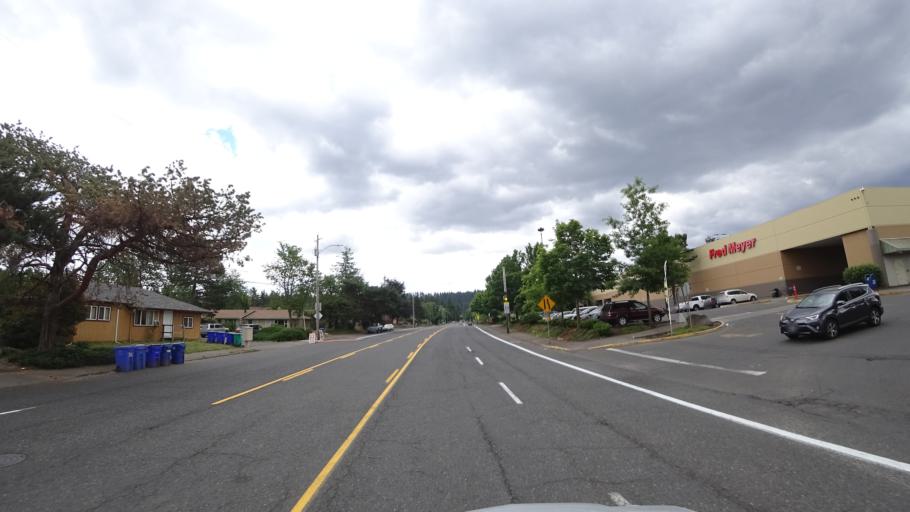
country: US
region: Oregon
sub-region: Clackamas County
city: Happy Valley
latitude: 45.5035
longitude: -122.5105
